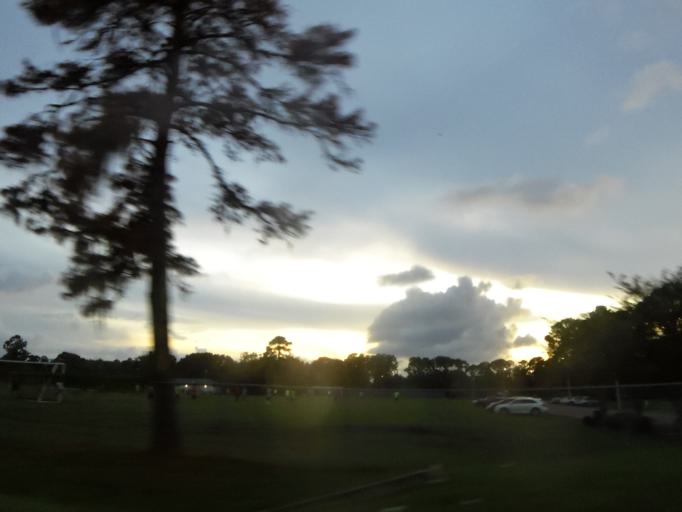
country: US
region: Florida
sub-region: Duval County
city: Jacksonville
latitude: 30.3770
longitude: -81.6069
